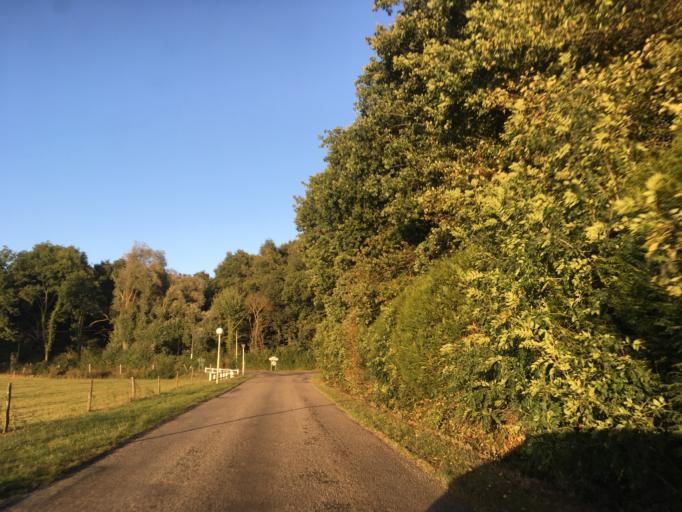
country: FR
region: Haute-Normandie
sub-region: Departement de l'Eure
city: Menilles
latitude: 49.0506
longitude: 1.3589
